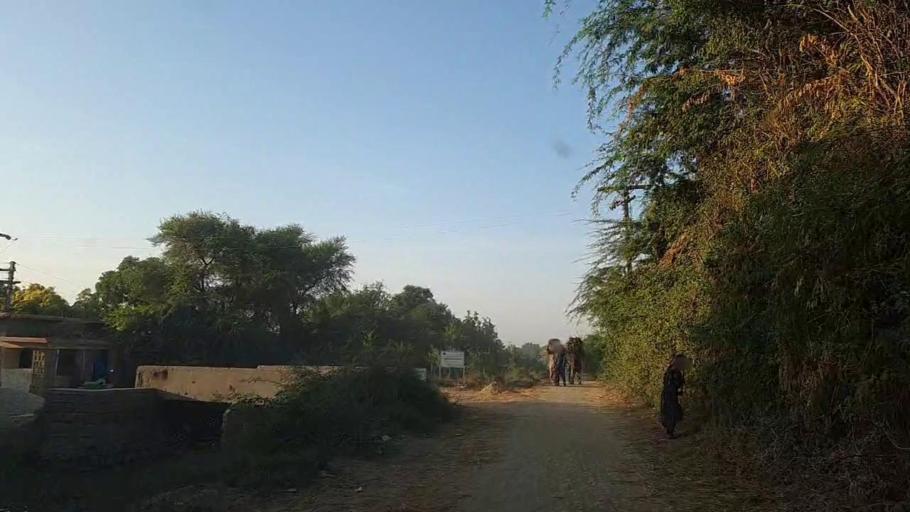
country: PK
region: Sindh
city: Mirpur Batoro
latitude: 24.7075
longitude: 68.2157
